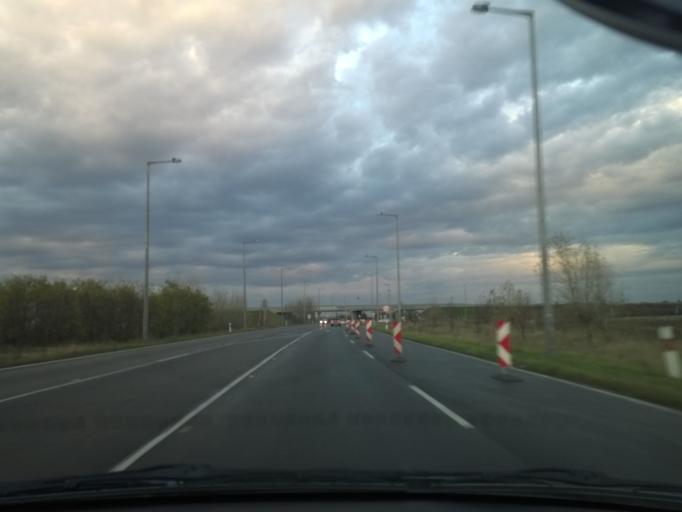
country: HU
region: Bacs-Kiskun
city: Dunavecse
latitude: 46.8944
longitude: 18.9833
